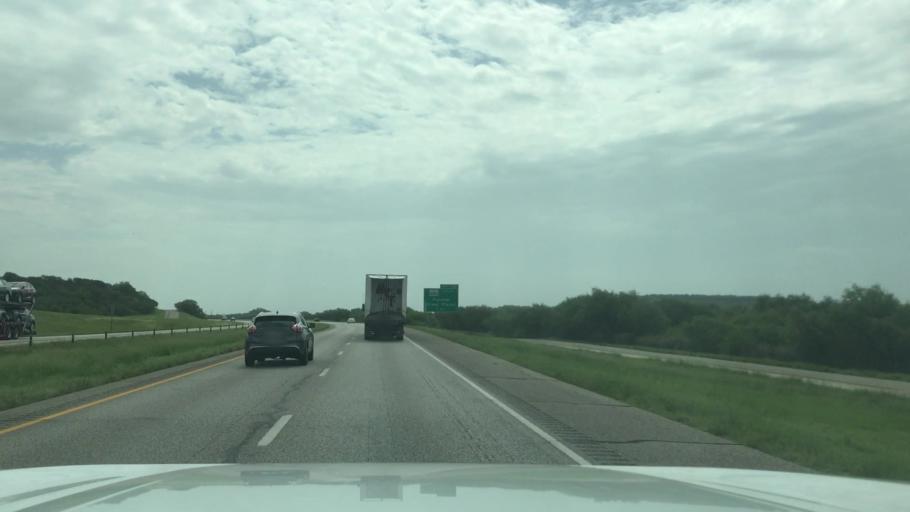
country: US
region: Texas
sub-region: Callahan County
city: Baird
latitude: 32.3707
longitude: -99.2175
